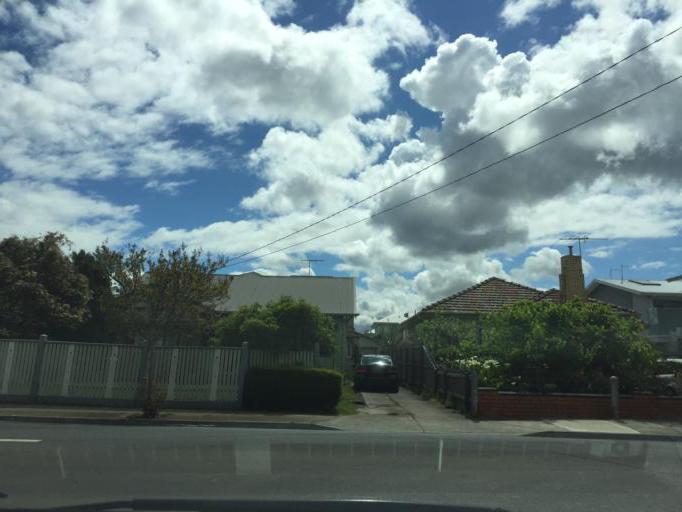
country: AU
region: Victoria
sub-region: Maribyrnong
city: West Footscray
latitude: -37.7961
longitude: 144.8652
